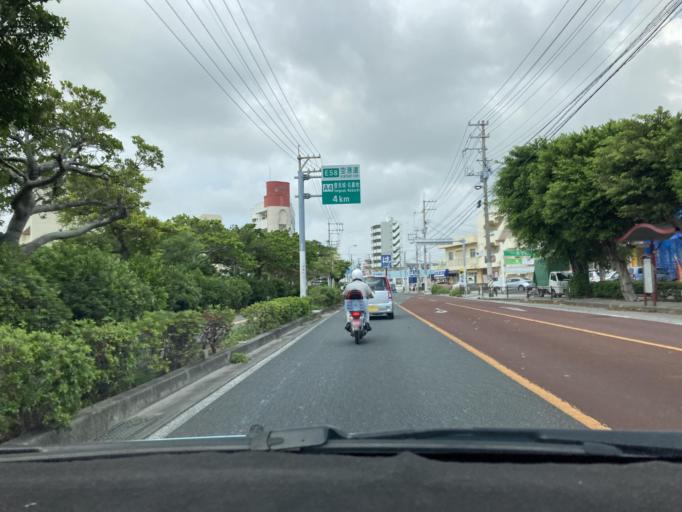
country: JP
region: Okinawa
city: Itoman
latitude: 26.1415
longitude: 127.6720
